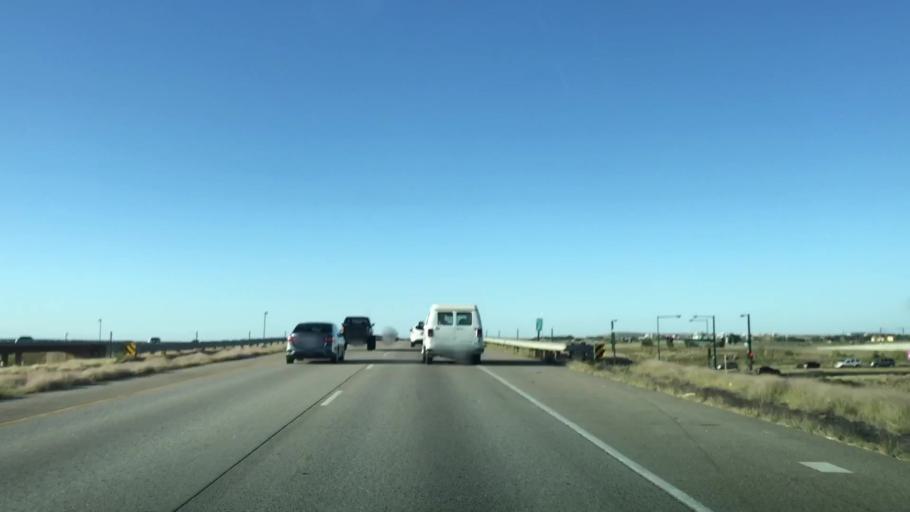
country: US
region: Colorado
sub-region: Adams County
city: Aurora
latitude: 39.7824
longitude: -104.7904
